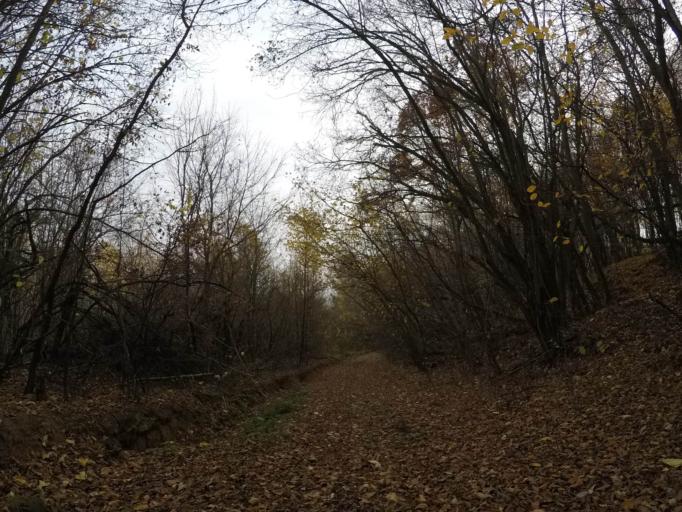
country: SK
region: Presovsky
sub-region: Okres Presov
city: Presov
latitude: 48.9383
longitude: 21.1692
